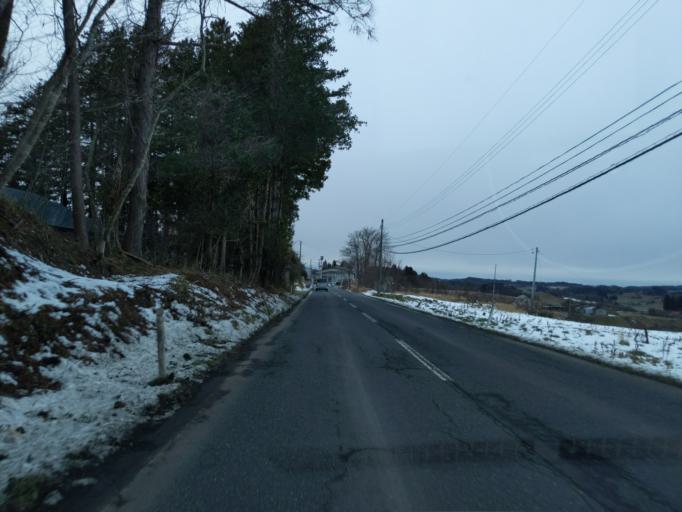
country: JP
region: Iwate
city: Mizusawa
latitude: 39.1824
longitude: 141.2521
